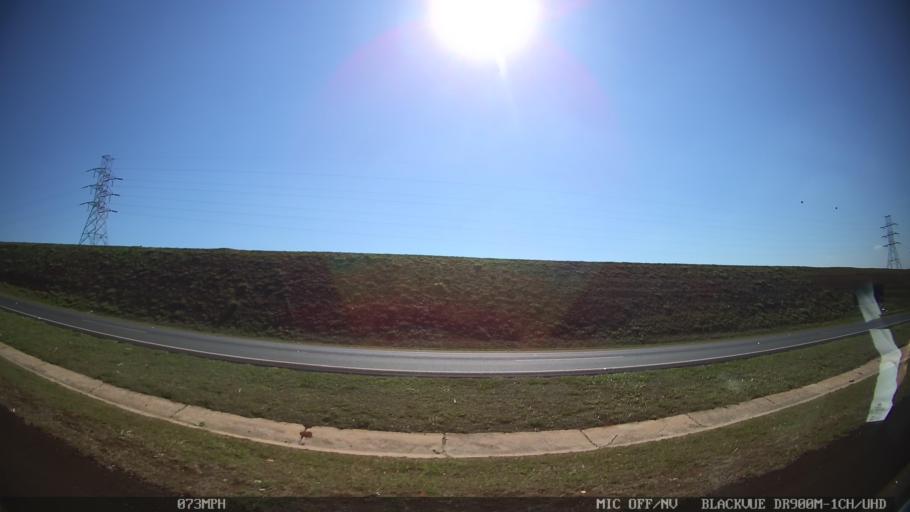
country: BR
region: Sao Paulo
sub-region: Ribeirao Preto
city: Ribeirao Preto
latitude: -21.1427
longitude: -47.8716
